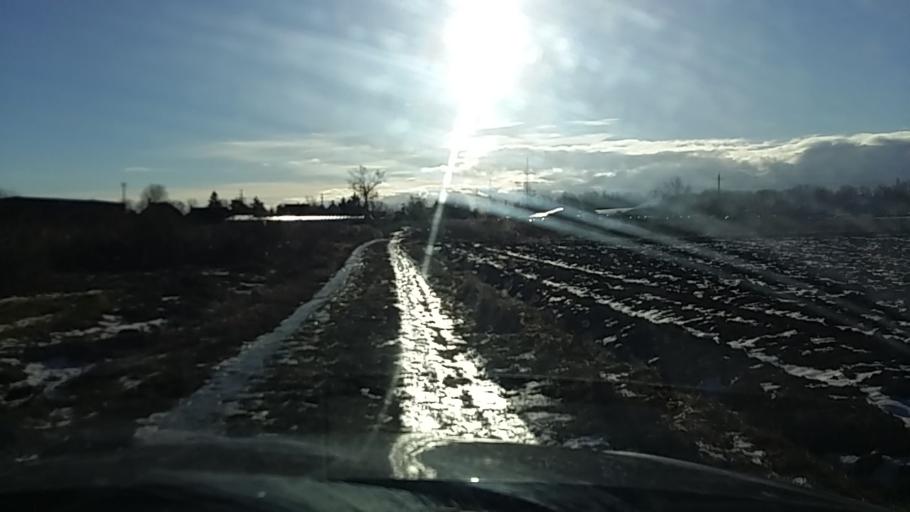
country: HU
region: Pest
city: Szigetszentmiklos
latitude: 47.3412
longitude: 19.0223
